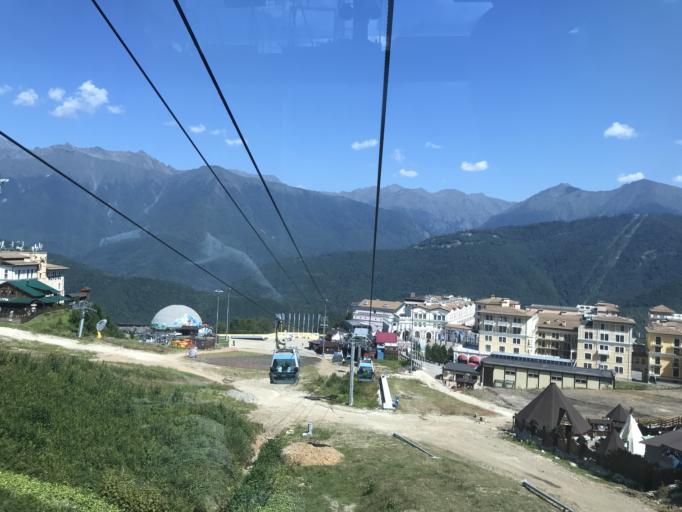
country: RU
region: Krasnodarskiy
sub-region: Sochi City
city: Krasnaya Polyana
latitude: 43.6671
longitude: 40.2576
